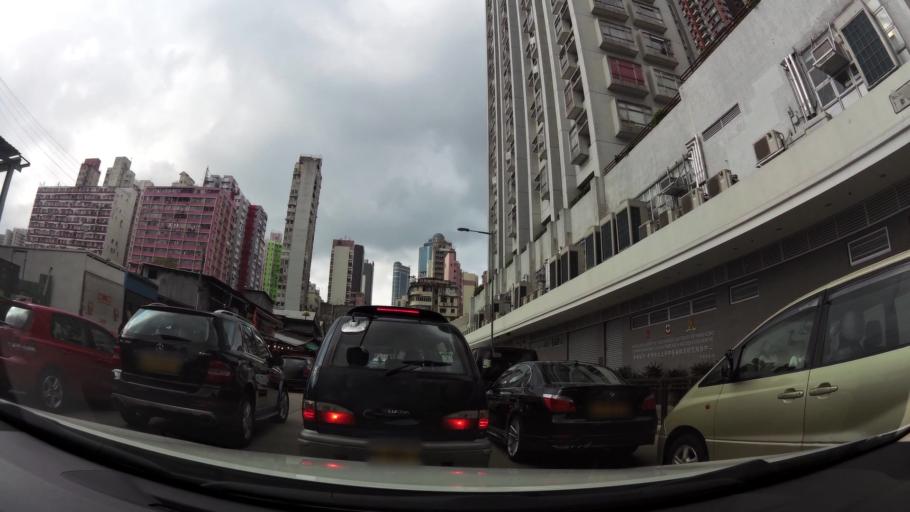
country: HK
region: Kowloon City
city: Kowloon
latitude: 22.3117
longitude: 114.1692
